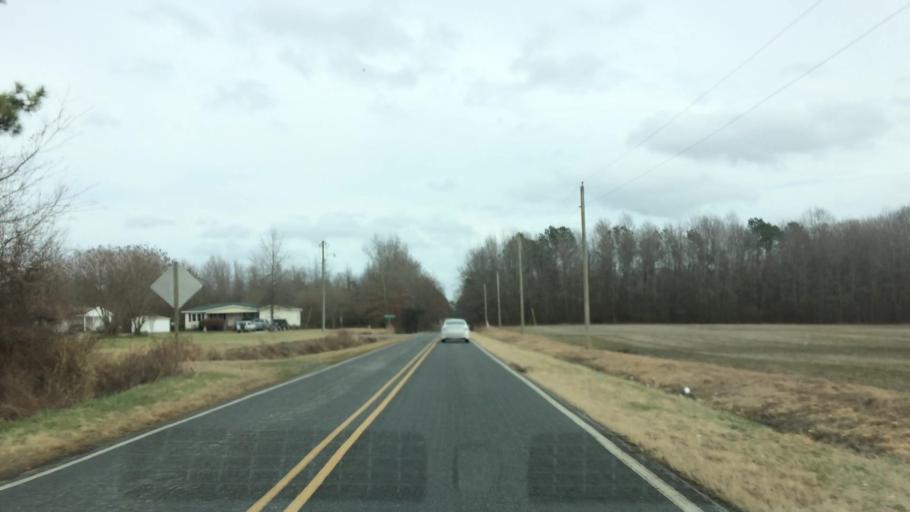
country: US
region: North Carolina
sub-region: Pitt County
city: Ayden
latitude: 35.4880
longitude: -77.3712
